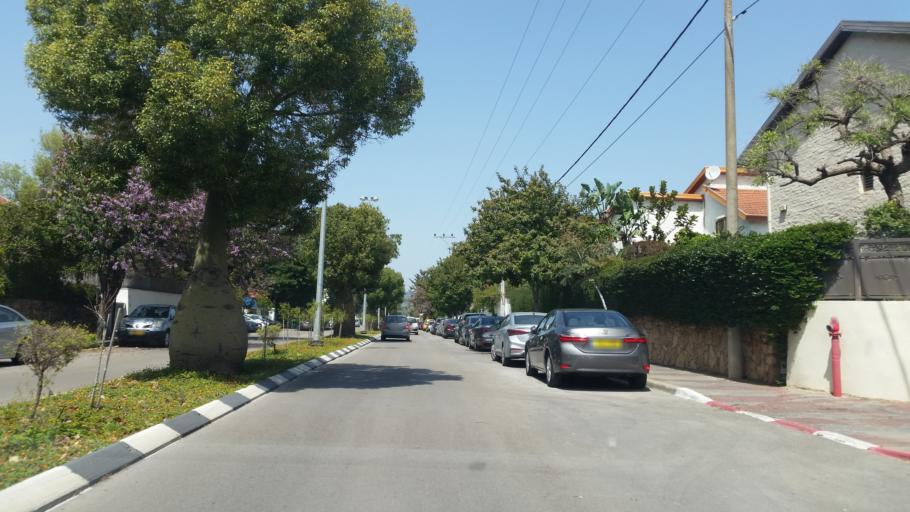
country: IL
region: Central District
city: Ra'anana
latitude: 32.1755
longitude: 34.8801
